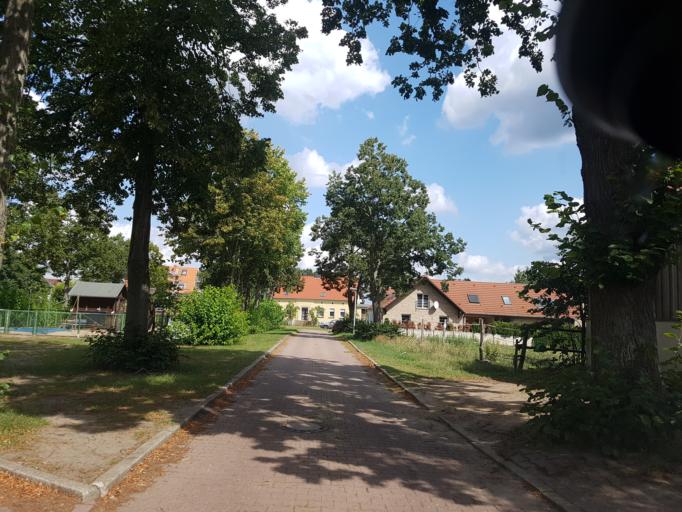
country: DE
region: Brandenburg
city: Borkwalde
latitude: 52.2885
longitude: 12.8386
